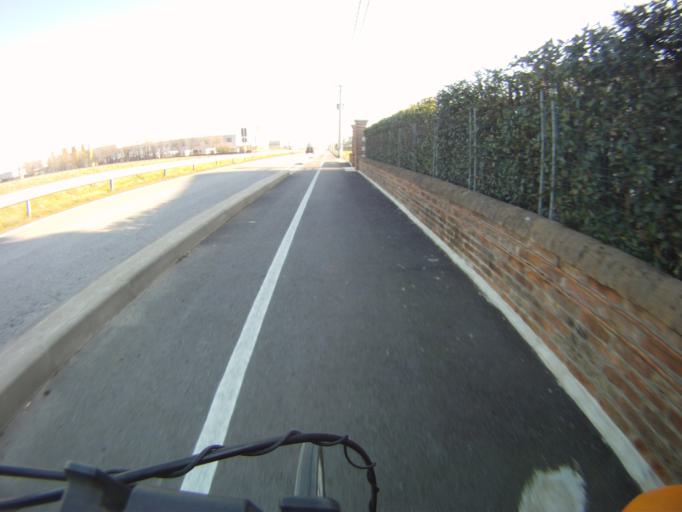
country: IT
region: Veneto
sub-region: Provincia di Padova
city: Brugine
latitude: 45.3090
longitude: 11.9892
